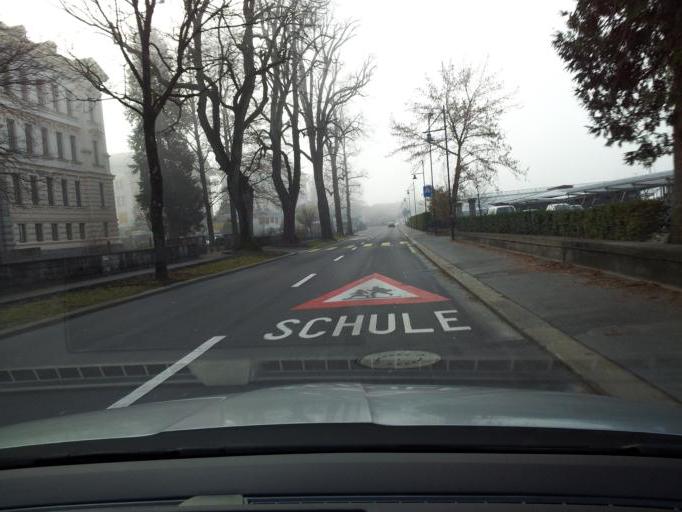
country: CH
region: Obwalden
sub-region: Obwalden
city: Sarnen
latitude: 46.8911
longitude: 8.2450
